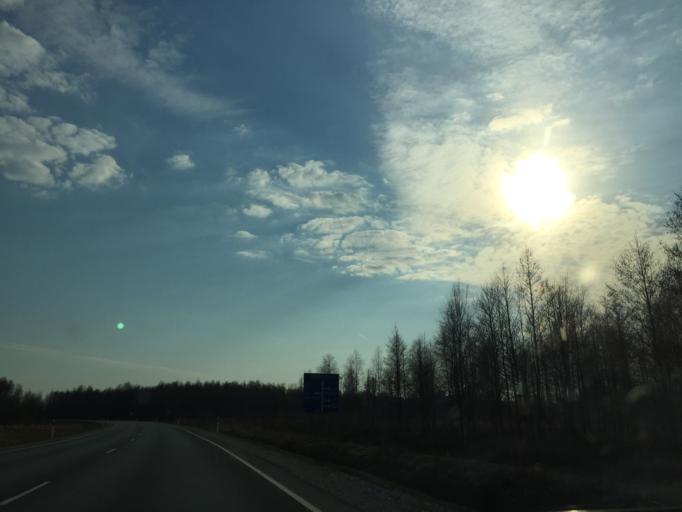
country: EE
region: Jogevamaa
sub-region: Mustvee linn
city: Mustvee
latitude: 58.8563
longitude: 26.9187
